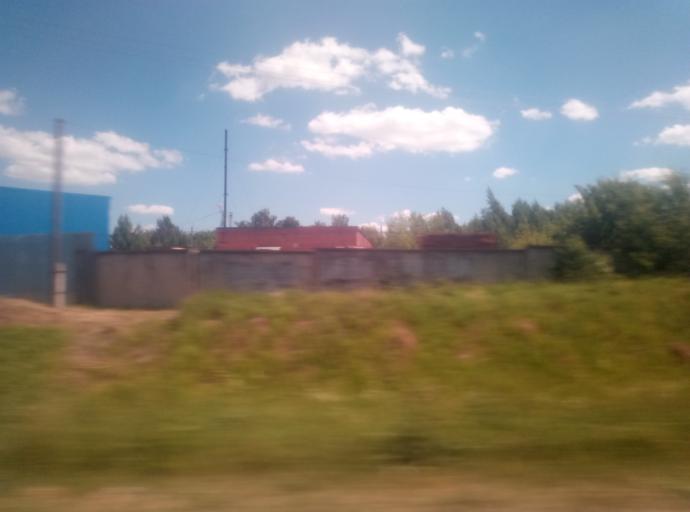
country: RU
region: Tula
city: Kireyevsk
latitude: 53.9339
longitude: 37.9455
